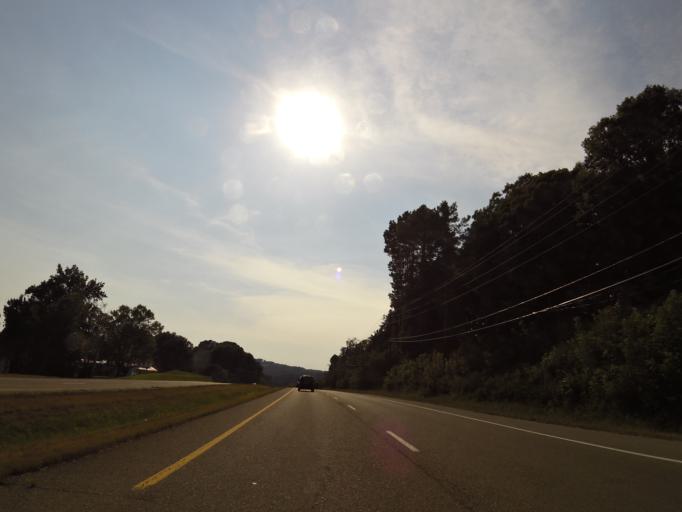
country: US
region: Tennessee
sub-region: Loudon County
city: Lenoir City
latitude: 35.8416
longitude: -84.3017
